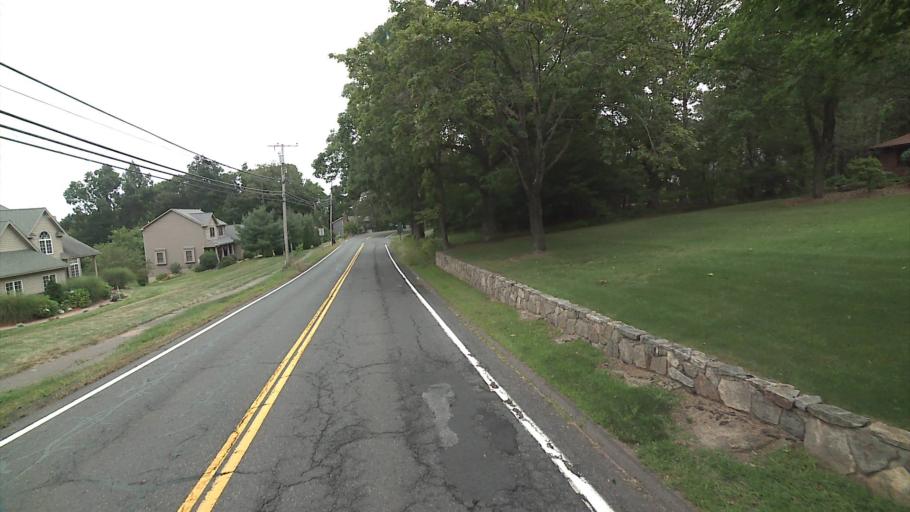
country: US
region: Connecticut
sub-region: Hartford County
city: Manchester
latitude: 41.8073
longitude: -72.4702
